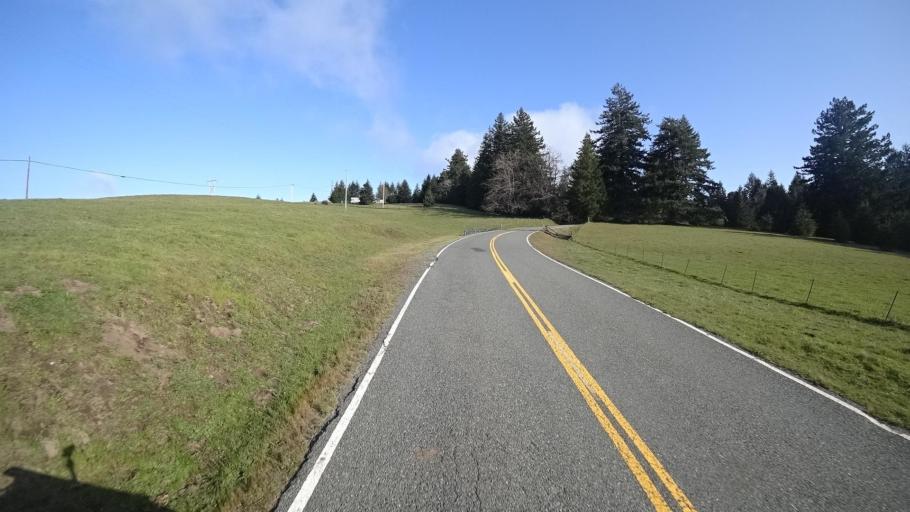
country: US
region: California
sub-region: Humboldt County
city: Blue Lake
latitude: 40.7214
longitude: -123.9429
